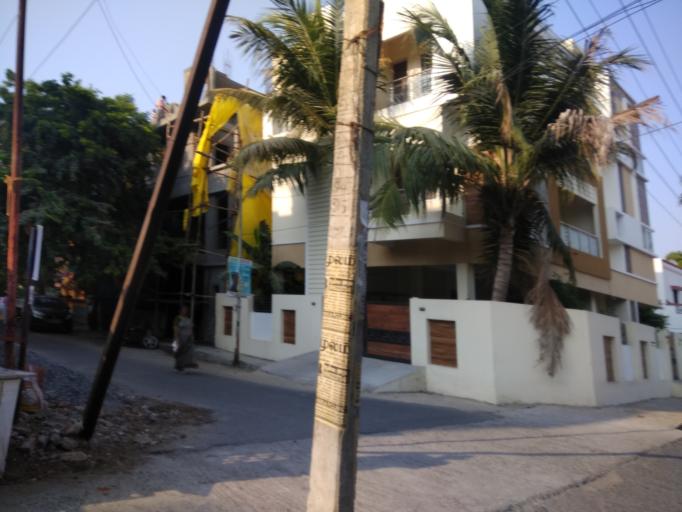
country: IN
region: Tamil Nadu
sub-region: Kancheepuram
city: Madipakkam
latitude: 12.9807
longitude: 80.1888
